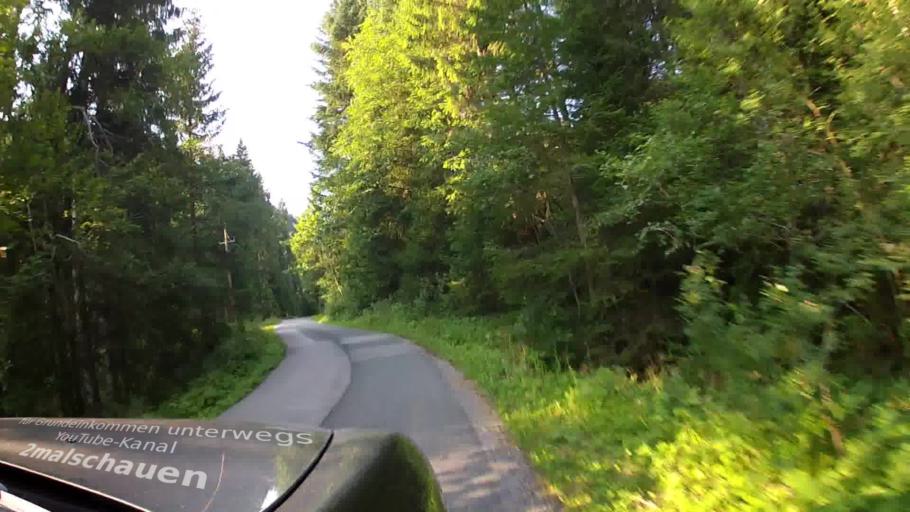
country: AT
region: Salzburg
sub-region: Politischer Bezirk Sankt Johann im Pongau
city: Eben im Pongau
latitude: 47.4331
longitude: 13.3806
